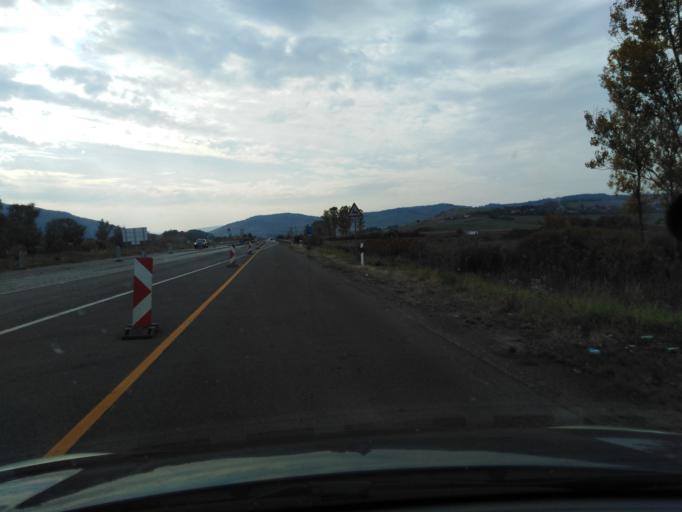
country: HU
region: Nograd
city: Matraverebely
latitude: 47.9781
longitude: 19.8067
